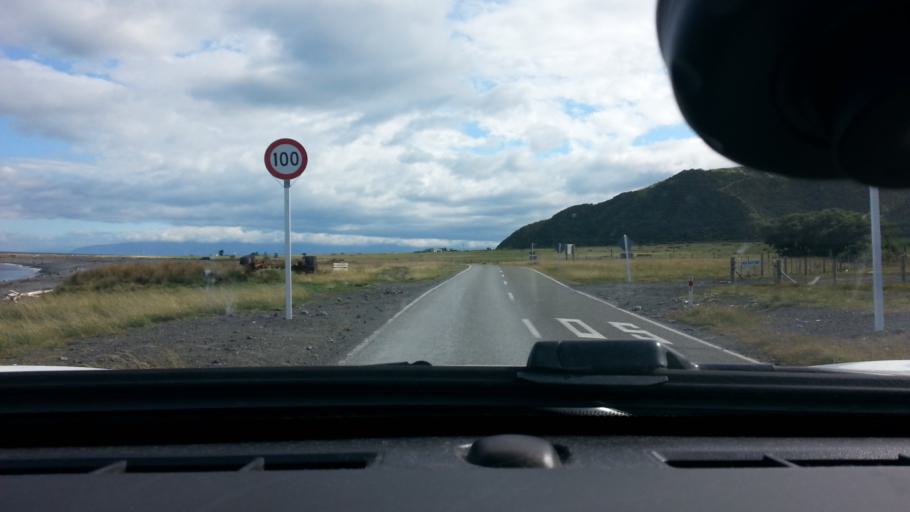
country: NZ
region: Wellington
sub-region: South Wairarapa District
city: Waipawa
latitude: -41.5844
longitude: 175.2340
